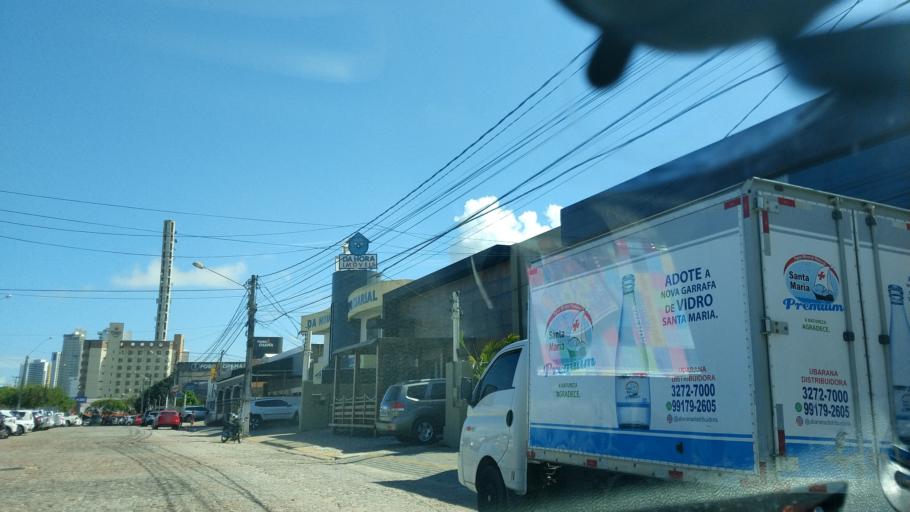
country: BR
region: Rio Grande do Norte
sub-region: Natal
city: Natal
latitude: -5.8684
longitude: -35.1826
